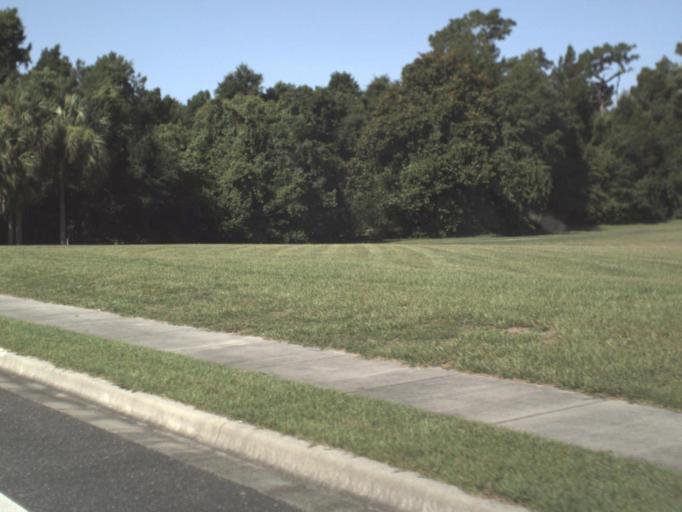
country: US
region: Florida
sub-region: Columbia County
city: Lake City
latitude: 30.1457
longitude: -82.6504
